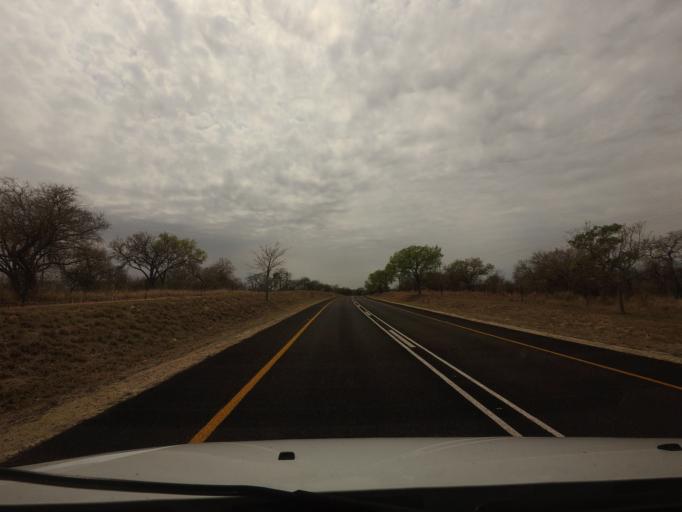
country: ZA
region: Limpopo
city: Thulamahashi
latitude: -24.5534
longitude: 31.1874
